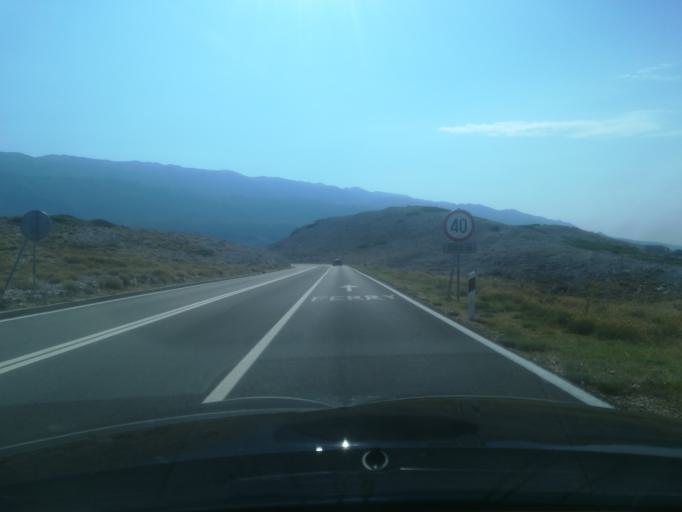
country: HR
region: Primorsko-Goranska
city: Banjol
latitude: 44.7047
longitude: 14.8466
